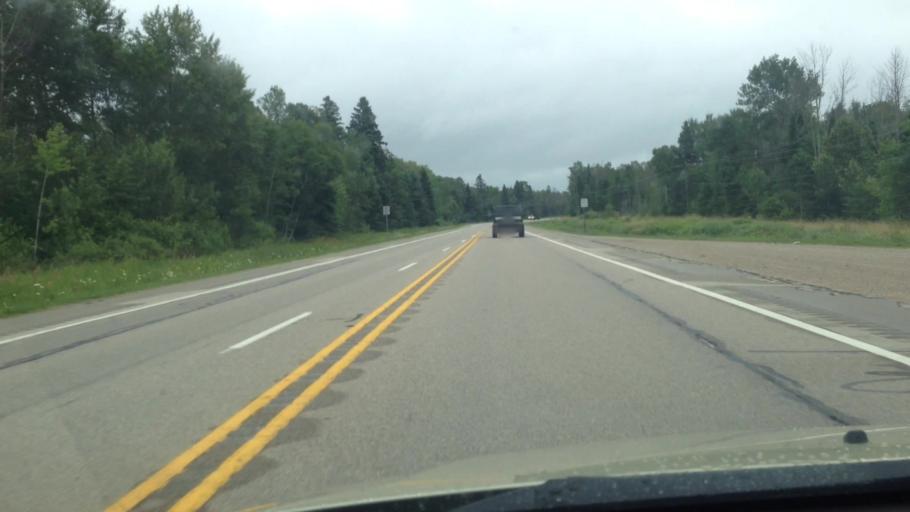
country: US
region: Michigan
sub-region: Schoolcraft County
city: Manistique
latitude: 45.9017
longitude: -86.5896
